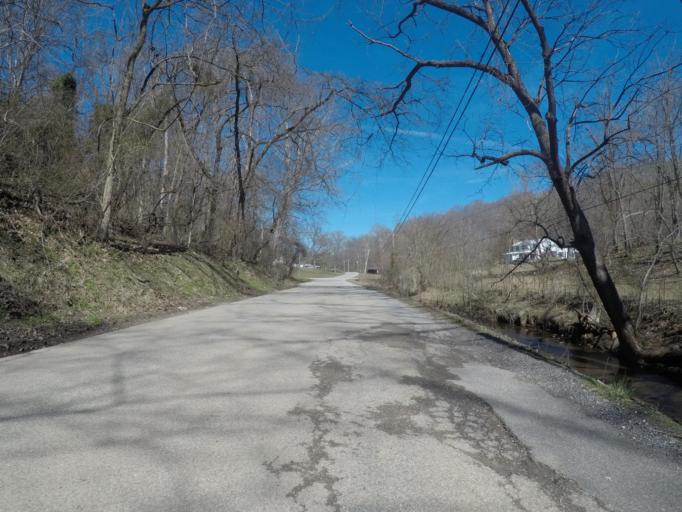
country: US
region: Ohio
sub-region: Lawrence County
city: Burlington
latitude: 38.4482
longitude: -82.5036
